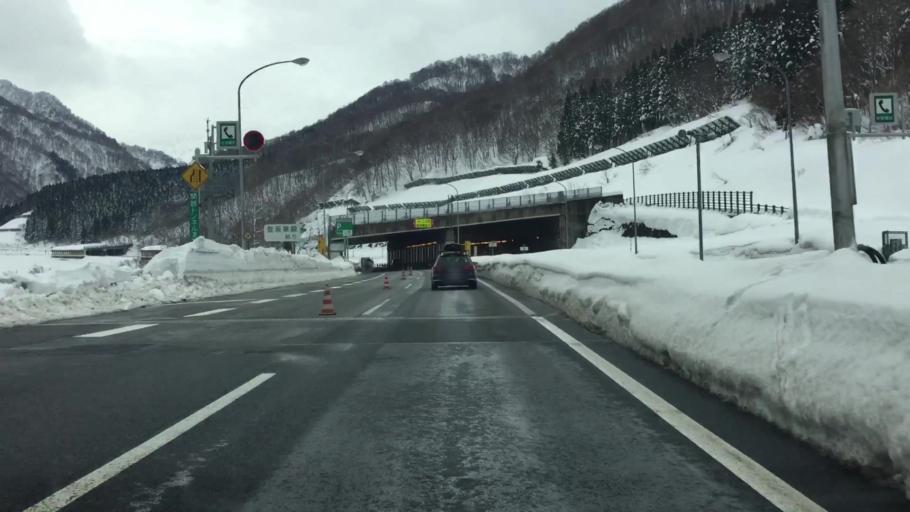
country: JP
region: Niigata
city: Shiozawa
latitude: 36.8721
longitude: 138.8648
